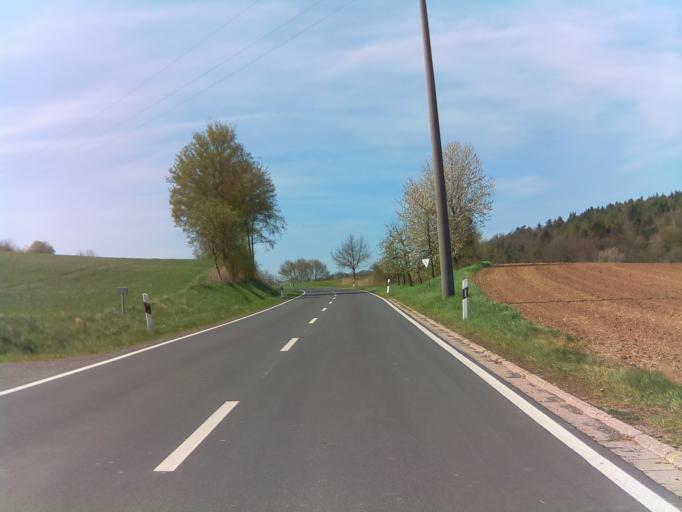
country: DE
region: Bavaria
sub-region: Regierungsbezirk Unterfranken
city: Burgpreppach
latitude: 50.1562
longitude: 10.6066
